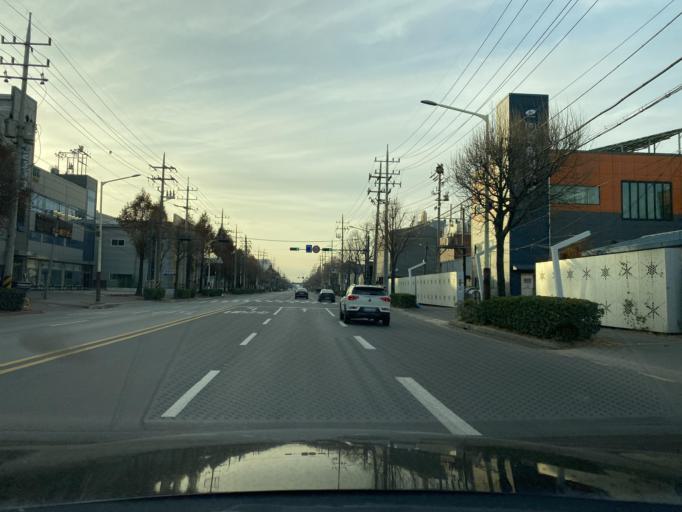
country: KR
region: Incheon
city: Incheon
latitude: 37.4992
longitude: 126.6583
